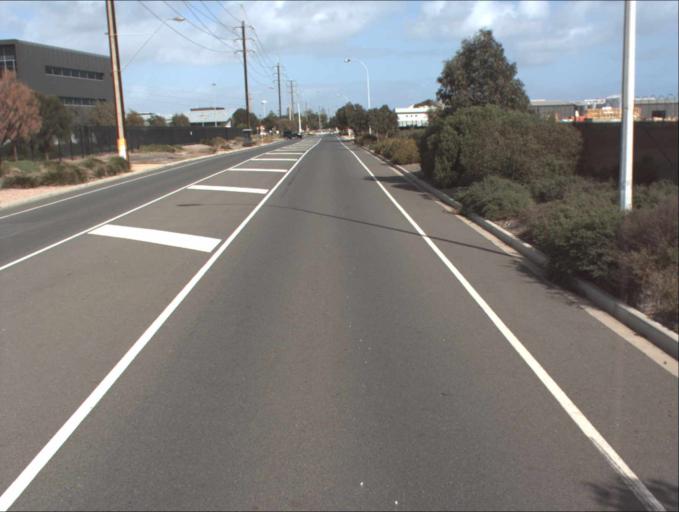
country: AU
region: South Australia
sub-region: Port Adelaide Enfield
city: Birkenhead
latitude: -34.7865
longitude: 138.5068
